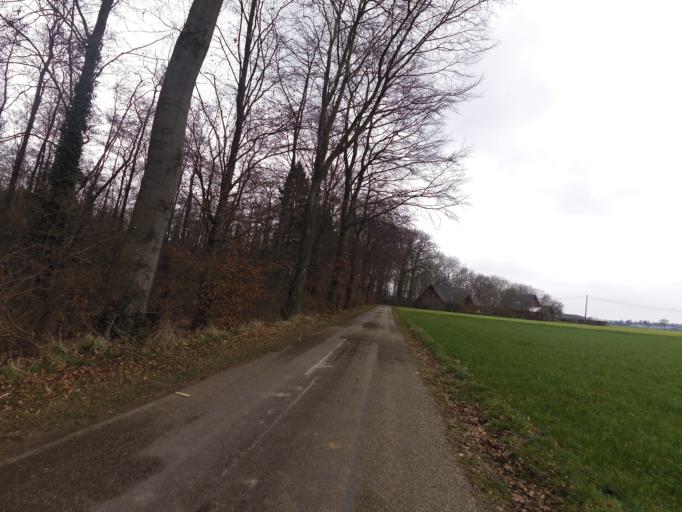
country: NL
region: Gelderland
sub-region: Oude IJsselstreek
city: Gendringen
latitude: 51.8685
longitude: 6.4029
